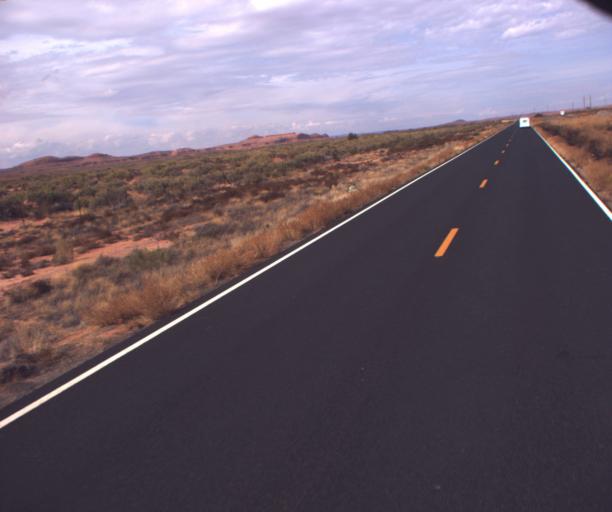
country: US
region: Arizona
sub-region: Apache County
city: Many Farms
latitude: 36.6709
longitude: -109.5992
